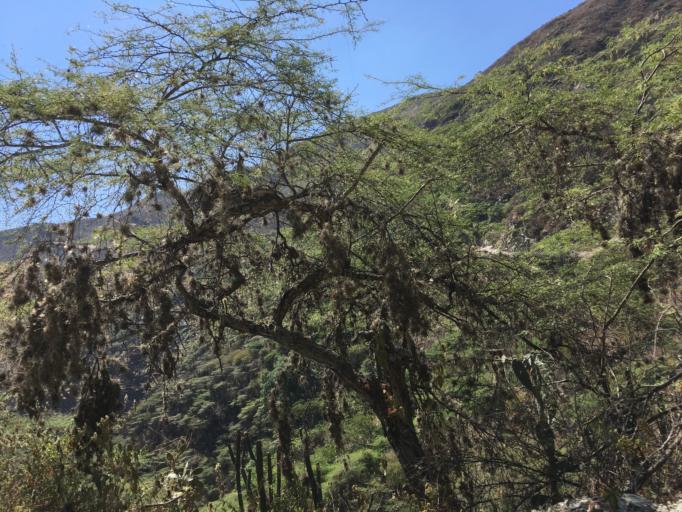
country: CO
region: Santander
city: Aratoca
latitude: 6.7769
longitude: -72.9942
